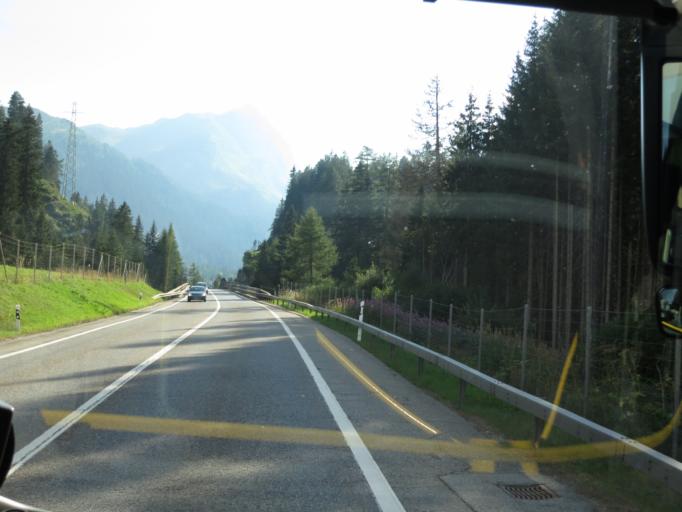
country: CH
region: Grisons
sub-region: Hinterrhein District
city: Hinterrhein
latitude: 46.5585
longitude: 9.3408
